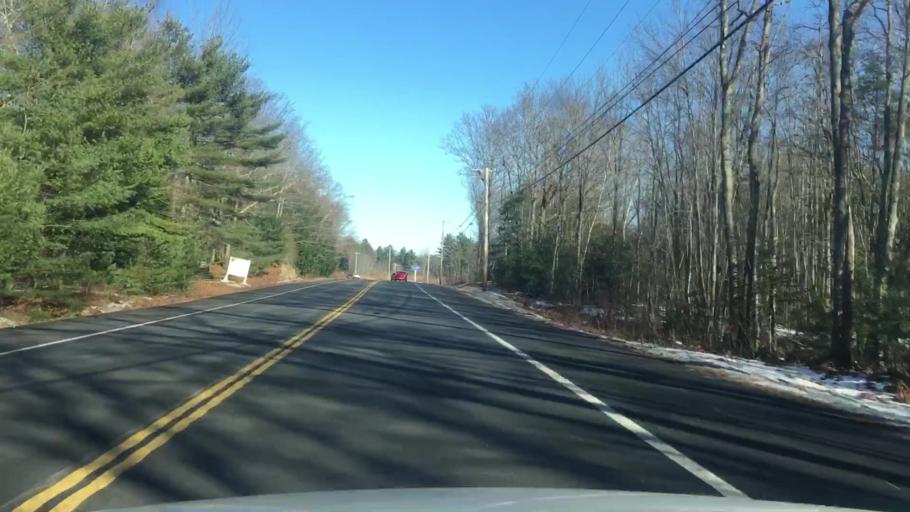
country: US
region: Maine
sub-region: York County
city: Arundel
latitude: 43.4349
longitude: -70.5050
